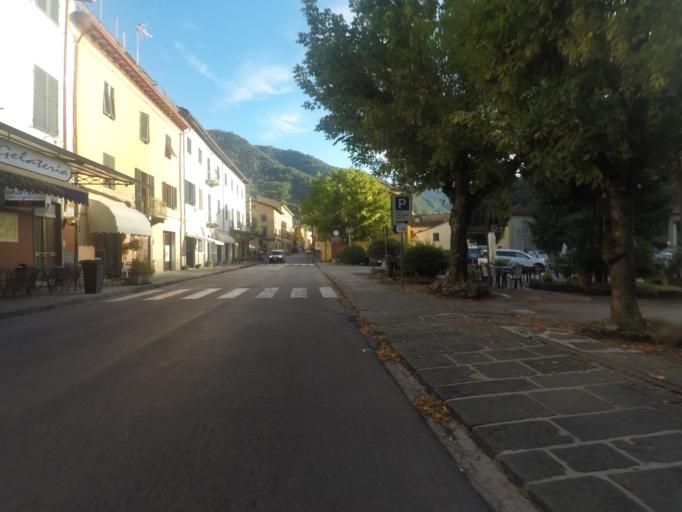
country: IT
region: Tuscany
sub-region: Provincia di Lucca
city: Bagni di Lucca
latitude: 44.0094
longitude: 10.5901
